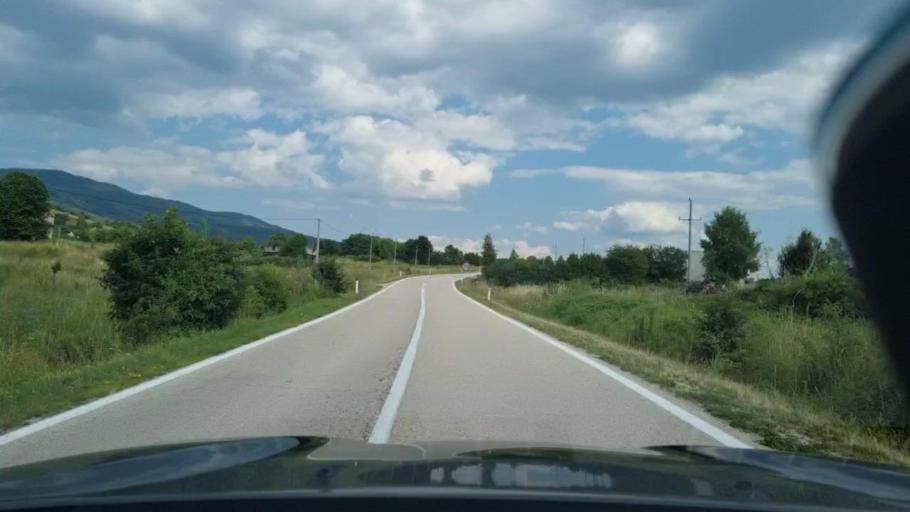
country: BA
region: Federation of Bosnia and Herzegovina
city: Bosansko Grahovo
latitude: 44.1244
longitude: 16.5254
